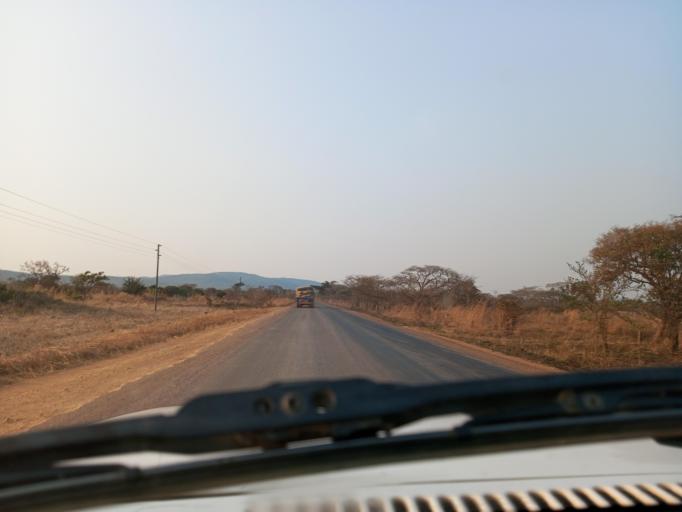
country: ZM
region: Northern
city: Mpika
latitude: -11.9276
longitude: 31.4179
